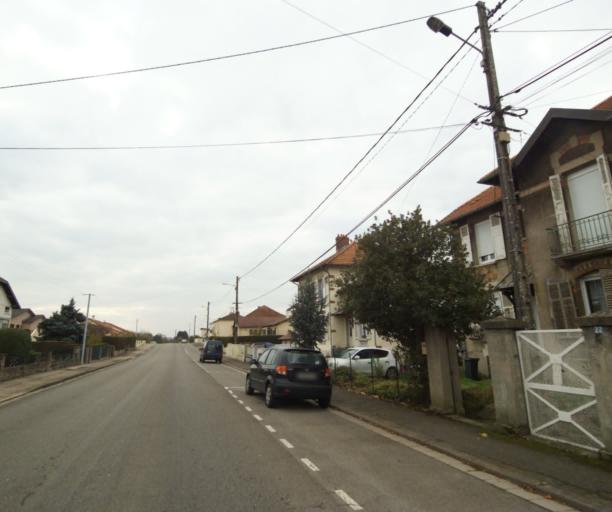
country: FR
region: Lorraine
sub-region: Departement de Meurthe-et-Moselle
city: Mancieulles
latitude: 49.2794
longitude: 5.8991
